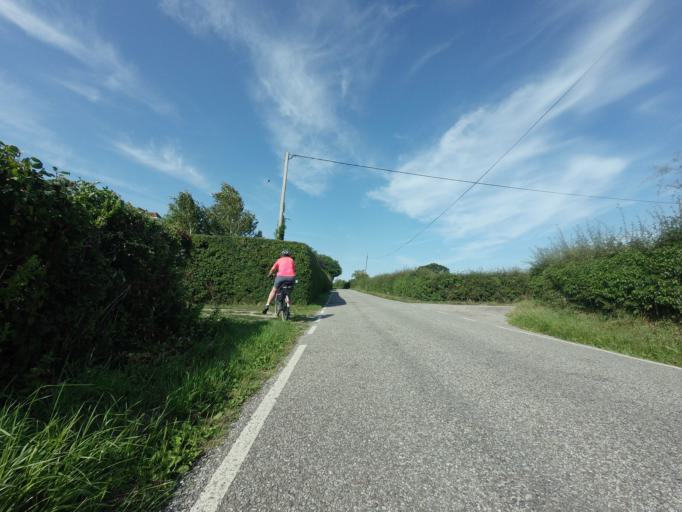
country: GB
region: England
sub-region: Kent
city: Tenterden
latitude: 51.0047
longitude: 0.6960
